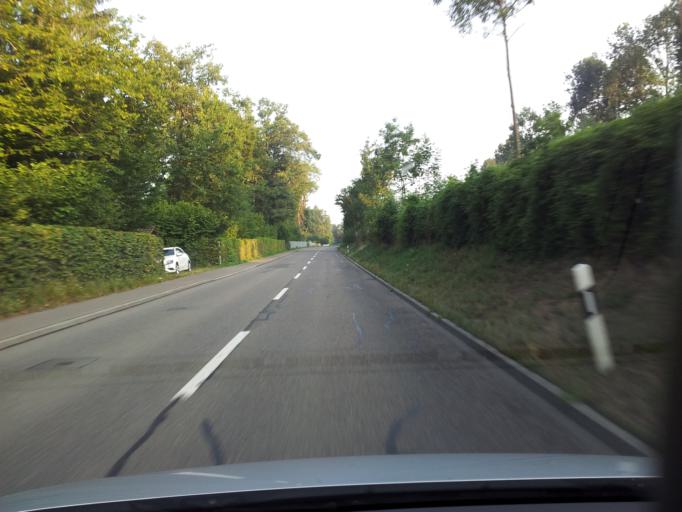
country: CH
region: Lucerne
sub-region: Sursee District
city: Schenkon
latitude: 47.1637
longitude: 8.1459
